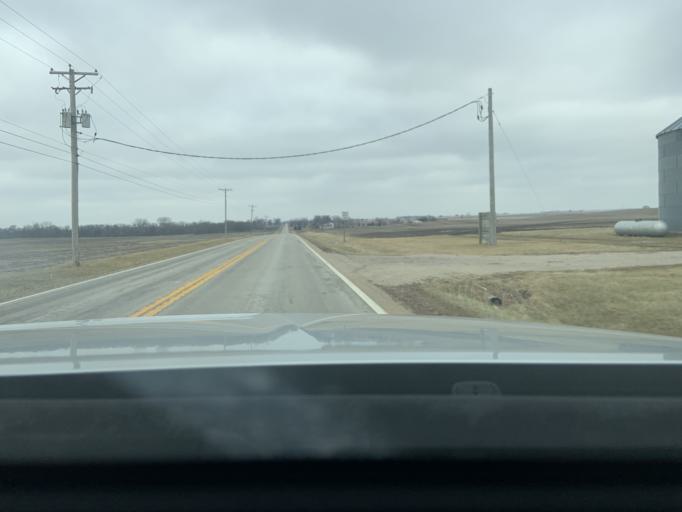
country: US
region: Illinois
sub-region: LaSalle County
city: Seneca
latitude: 41.3491
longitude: -88.6119
